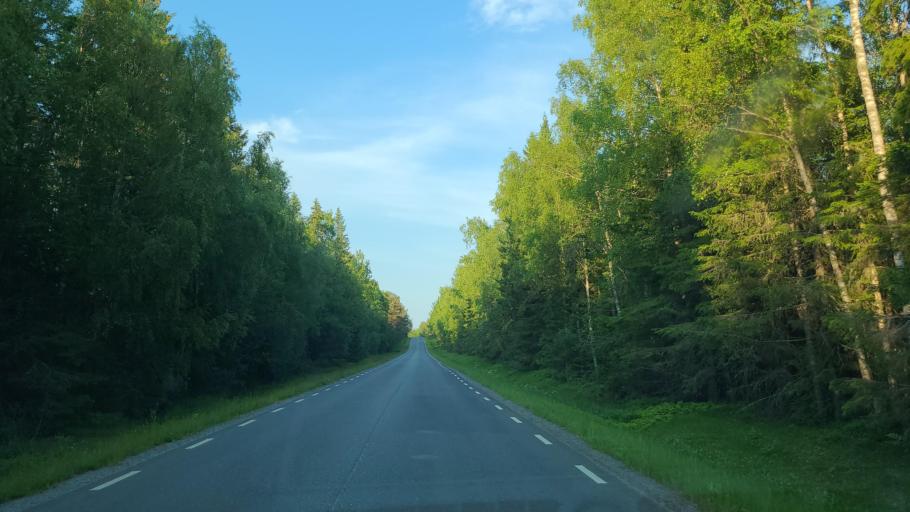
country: SE
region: Vaesterbotten
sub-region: Skelleftea Kommun
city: Burea
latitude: 64.4517
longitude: 21.5626
